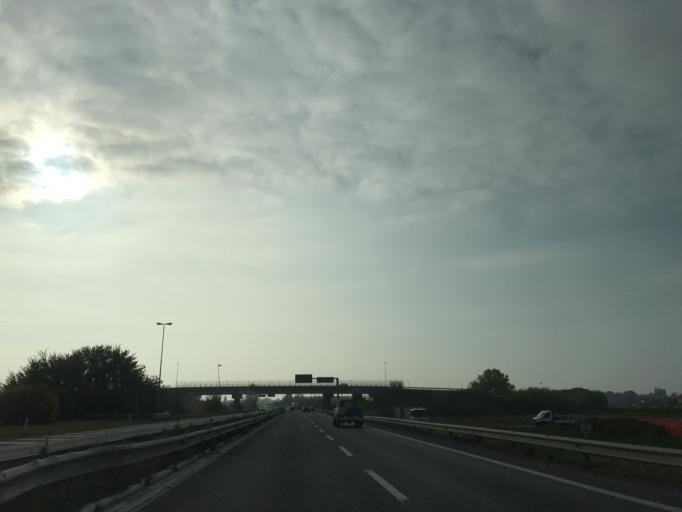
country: IT
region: Emilia-Romagna
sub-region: Forli-Cesena
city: Cesenatico
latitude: 44.1806
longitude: 12.4120
